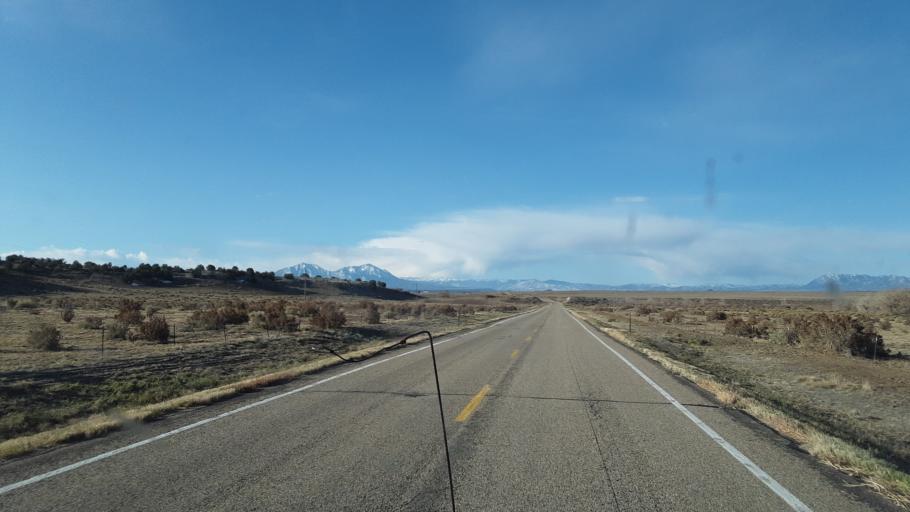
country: US
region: Colorado
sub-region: Huerfano County
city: Walsenburg
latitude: 37.6853
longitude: -104.6446
